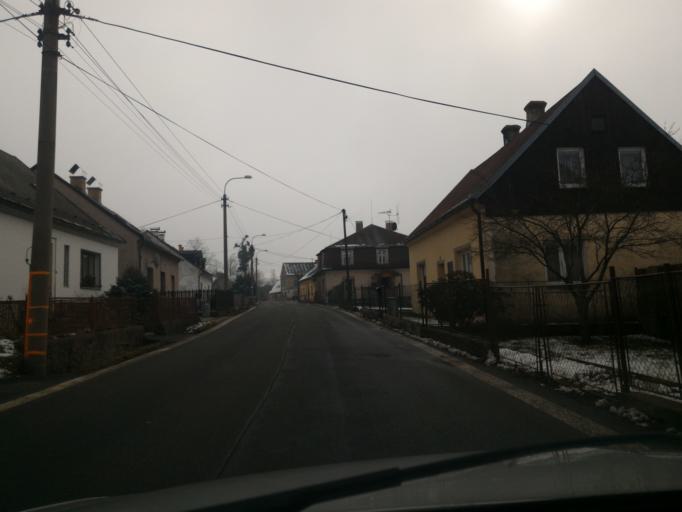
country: CZ
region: Liberecky
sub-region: Okres Liberec
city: Hejnice
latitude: 50.8763
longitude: 15.1903
